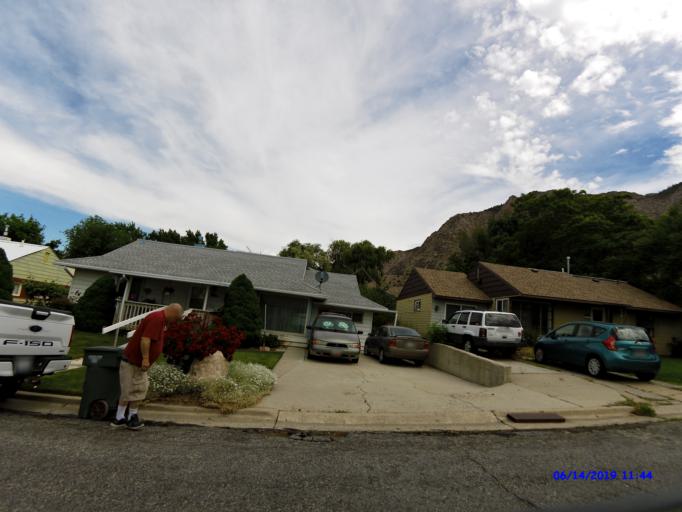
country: US
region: Utah
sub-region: Weber County
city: Ogden
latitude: 41.2541
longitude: -111.9448
